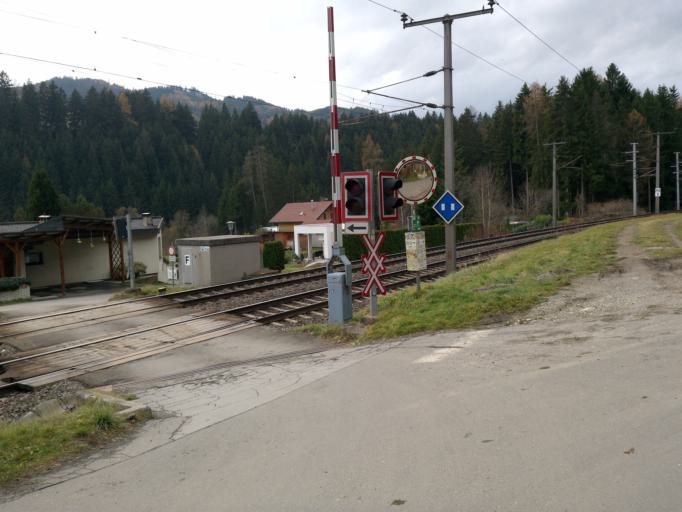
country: AT
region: Styria
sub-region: Politischer Bezirk Murtal
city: Judenburg
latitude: 47.1747
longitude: 14.6500
